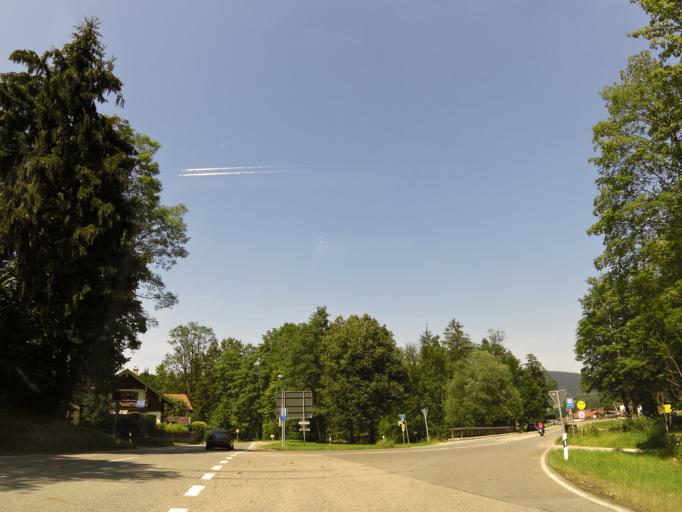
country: DE
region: Bavaria
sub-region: Upper Bavaria
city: Ruhpolding
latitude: 47.7396
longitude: 12.6588
